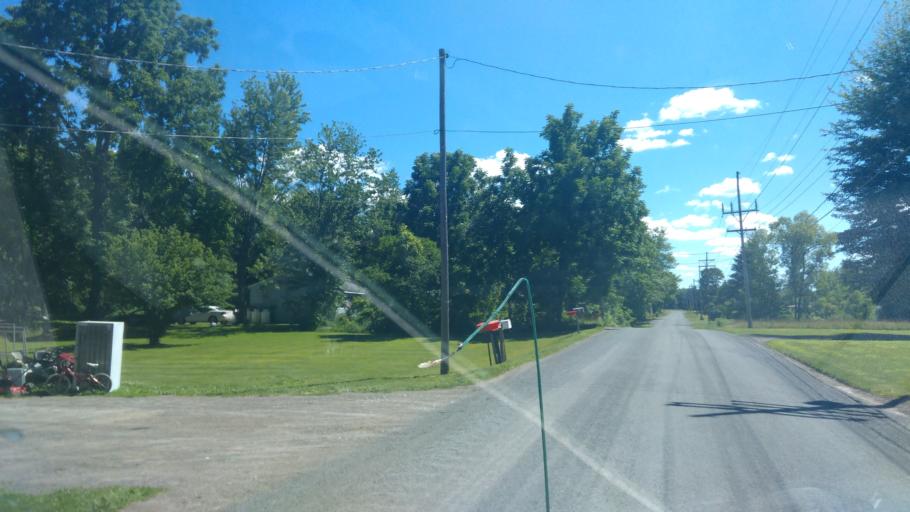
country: US
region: New York
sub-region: Wayne County
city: Sodus
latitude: 43.2223
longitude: -77.0236
